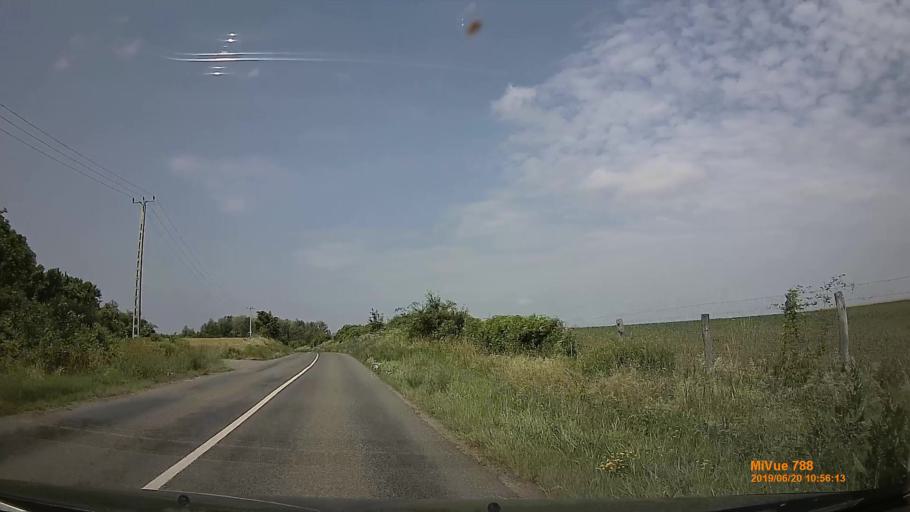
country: HU
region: Baranya
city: Mecseknadasd
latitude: 46.1564
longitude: 18.5395
